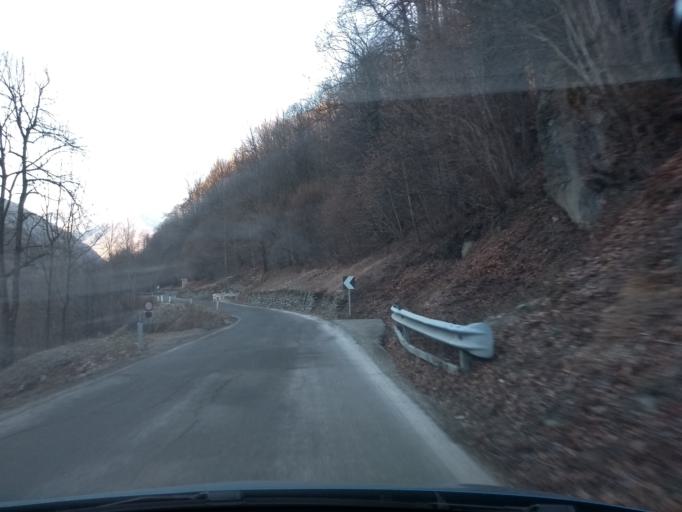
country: IT
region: Piedmont
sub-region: Provincia di Torino
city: Viu
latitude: 45.2323
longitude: 7.3546
